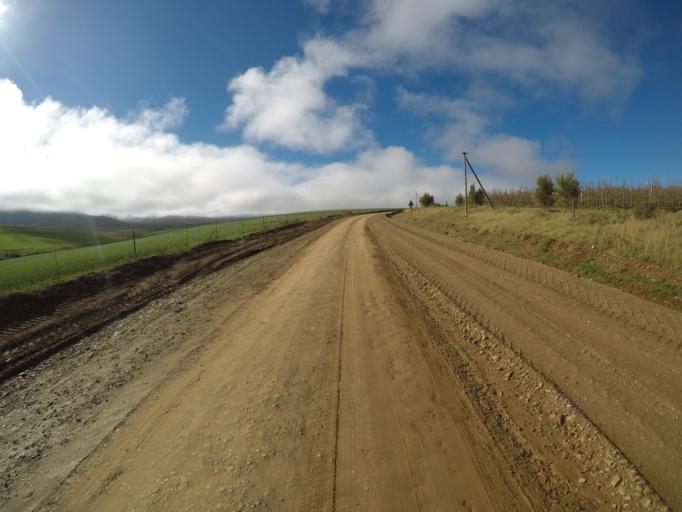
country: ZA
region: Western Cape
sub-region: Overberg District Municipality
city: Caledon
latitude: -34.1094
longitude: 19.7551
